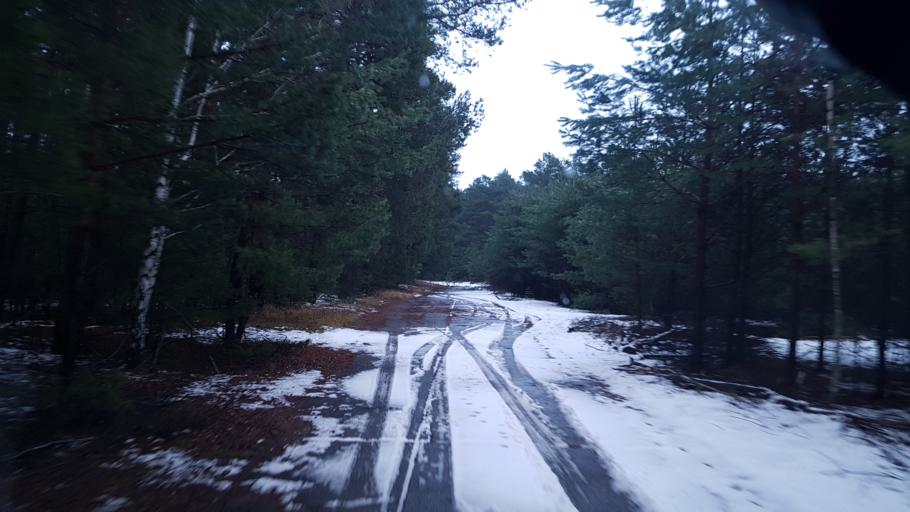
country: DE
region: Brandenburg
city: Janschwalde
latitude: 51.8851
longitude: 14.5444
